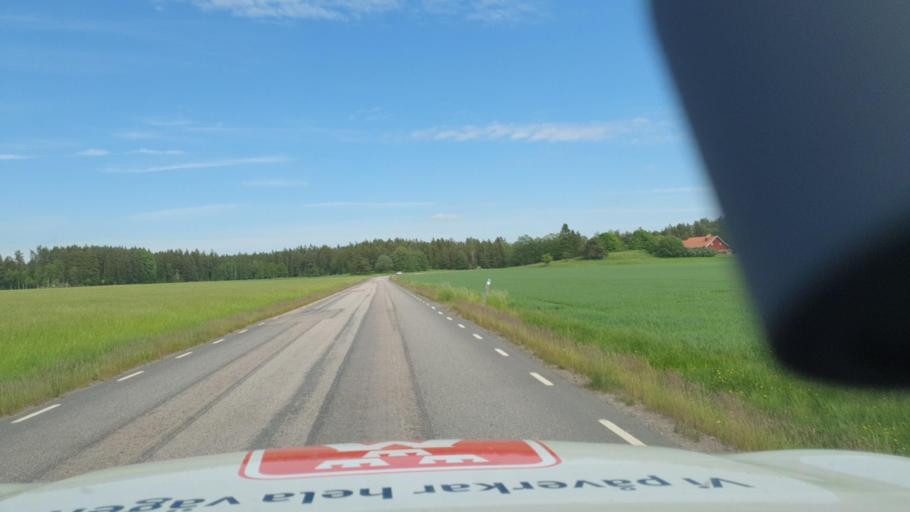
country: SE
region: Vaestra Goetaland
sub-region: Essunga Kommun
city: Nossebro
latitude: 58.2211
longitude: 12.6353
